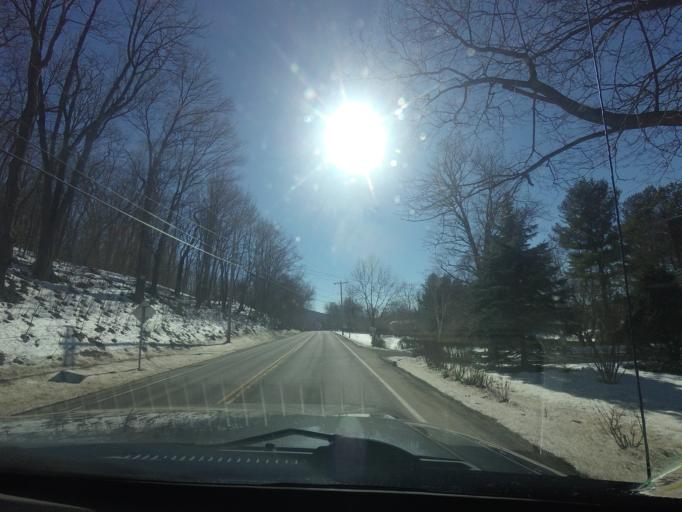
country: US
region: New York
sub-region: Saratoga County
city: Waterford
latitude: 42.8388
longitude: -73.6248
